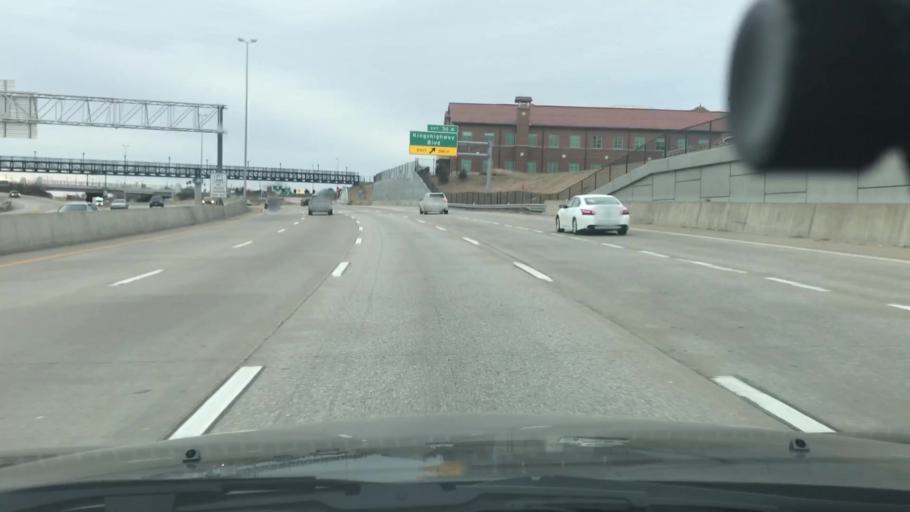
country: US
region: Missouri
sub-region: Saint Louis County
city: University City
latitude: 38.6322
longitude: -90.2615
